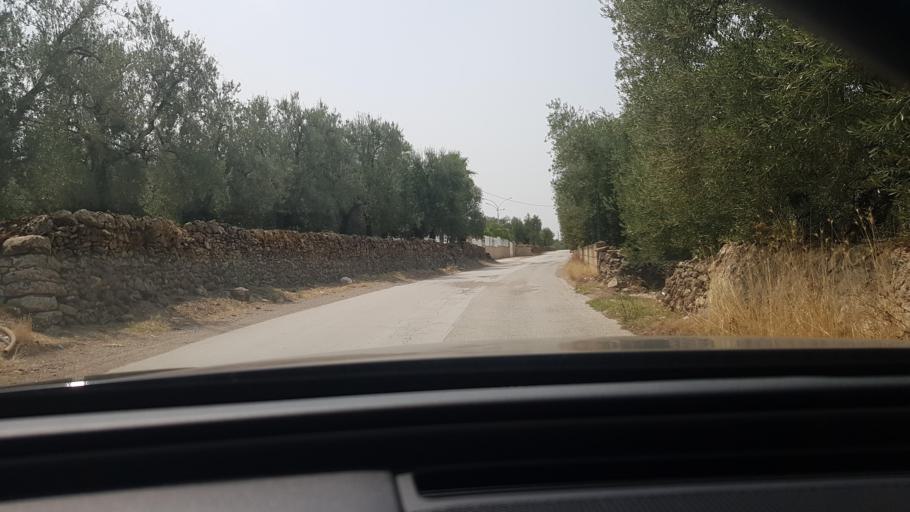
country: IT
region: Apulia
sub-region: Provincia di Barletta - Andria - Trani
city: Andria
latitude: 41.2248
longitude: 16.2672
